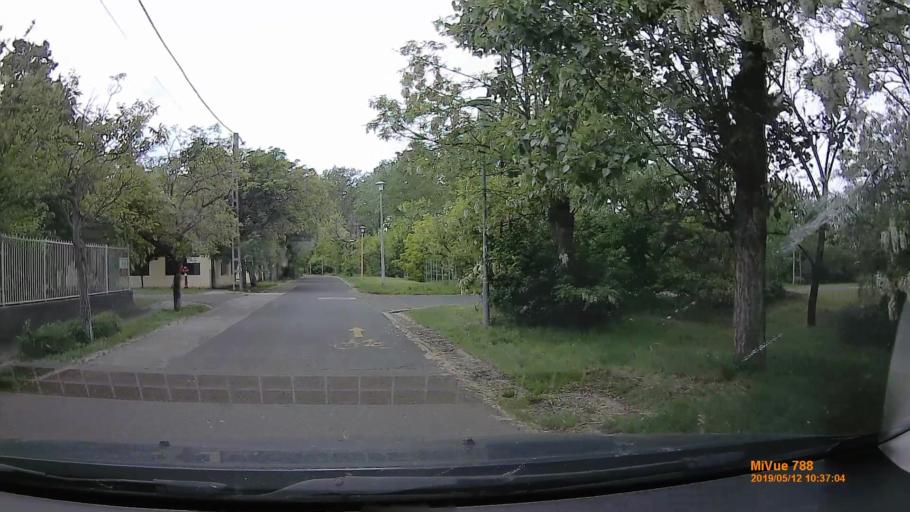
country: HU
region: Budapest
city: Budapest XVII. keruelet
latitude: 47.4849
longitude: 19.2221
